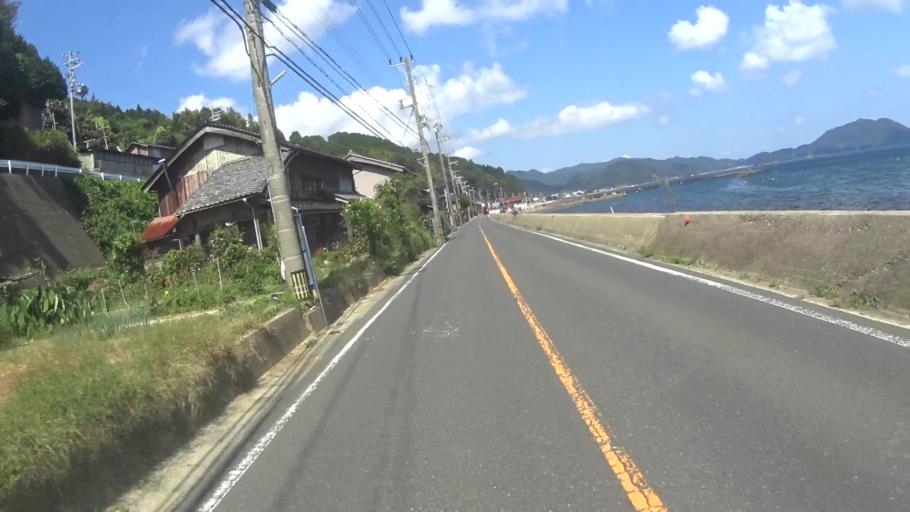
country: JP
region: Kyoto
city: Miyazu
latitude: 35.6470
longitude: 135.2518
